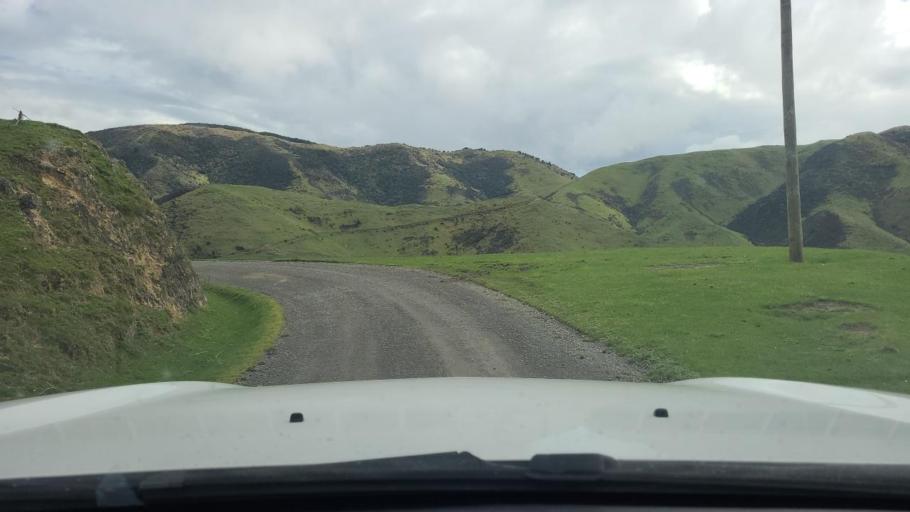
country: NZ
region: Wellington
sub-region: South Wairarapa District
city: Waipawa
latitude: -41.3659
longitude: 175.3857
